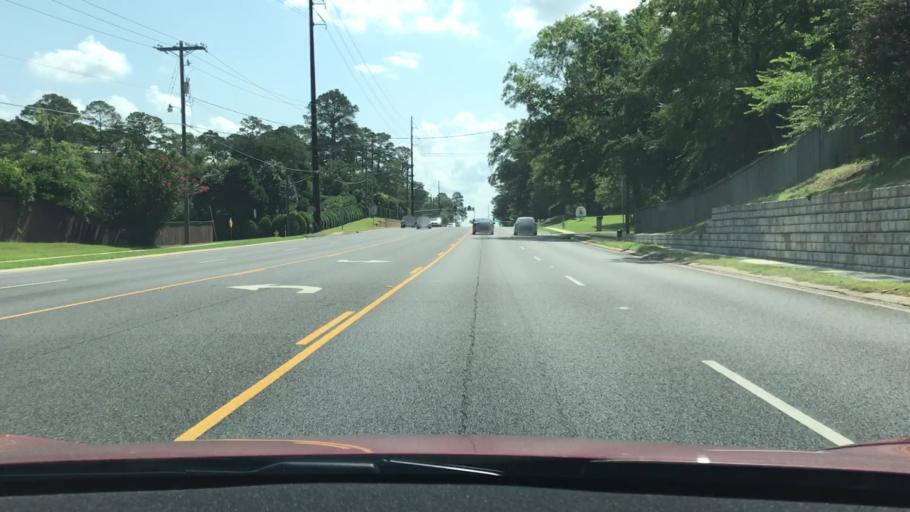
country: US
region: Louisiana
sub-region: Bossier Parish
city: Bossier City
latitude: 32.4428
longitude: -93.7379
